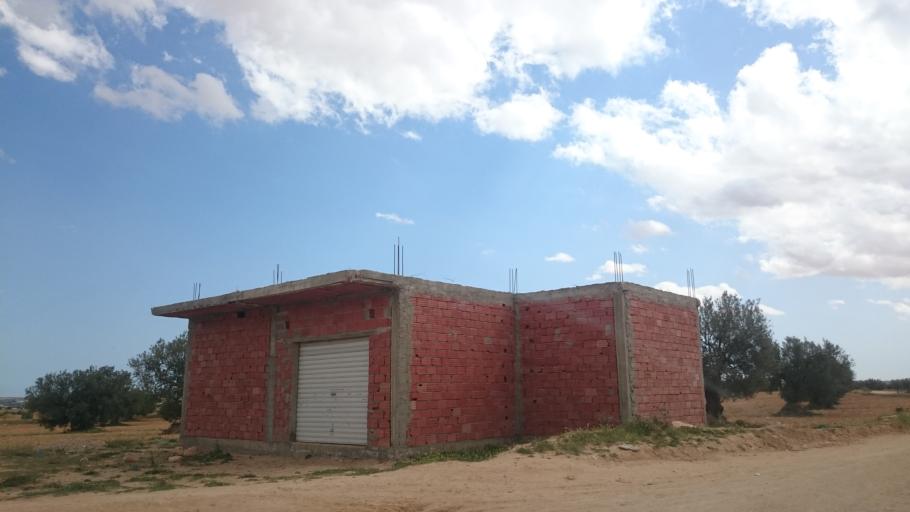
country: TN
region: Safaqis
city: Sfax
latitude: 34.7519
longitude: 10.4881
